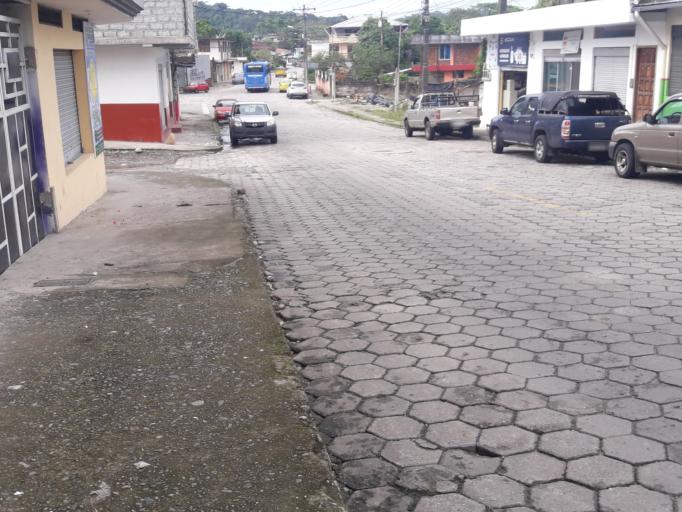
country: EC
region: Napo
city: Tena
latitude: -0.9984
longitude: -77.8148
